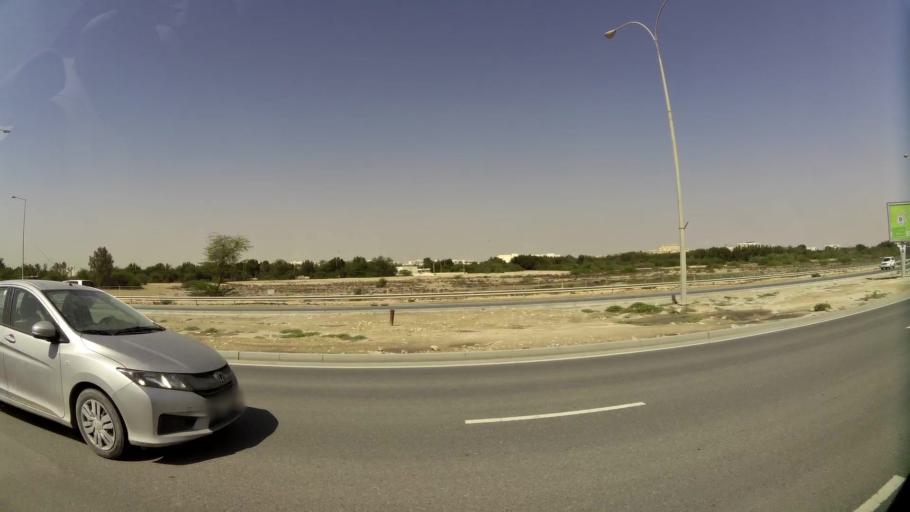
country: QA
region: Baladiyat ad Dawhah
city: Doha
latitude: 25.3685
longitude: 51.4977
